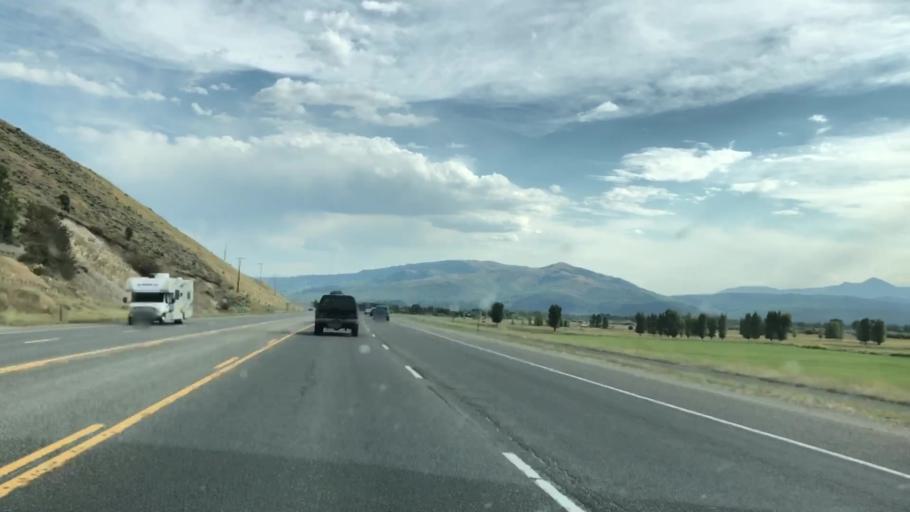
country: US
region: Wyoming
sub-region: Teton County
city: Rafter J Ranch
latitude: 43.4475
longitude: -110.7903
